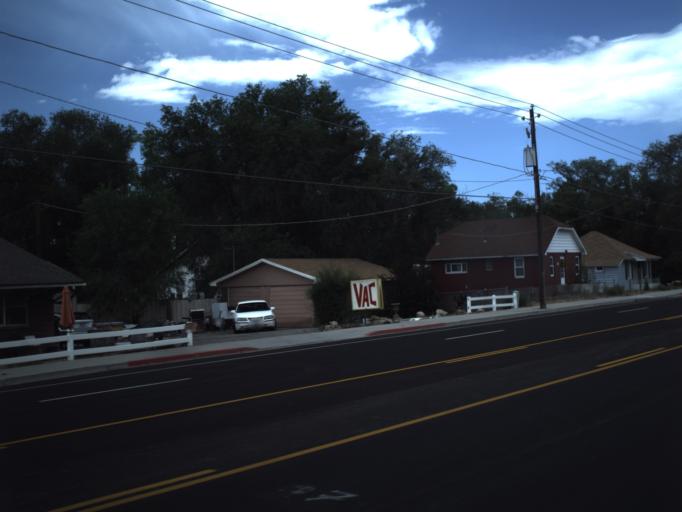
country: US
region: Utah
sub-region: Carbon County
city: Wellington
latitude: 39.5425
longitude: -110.7284
